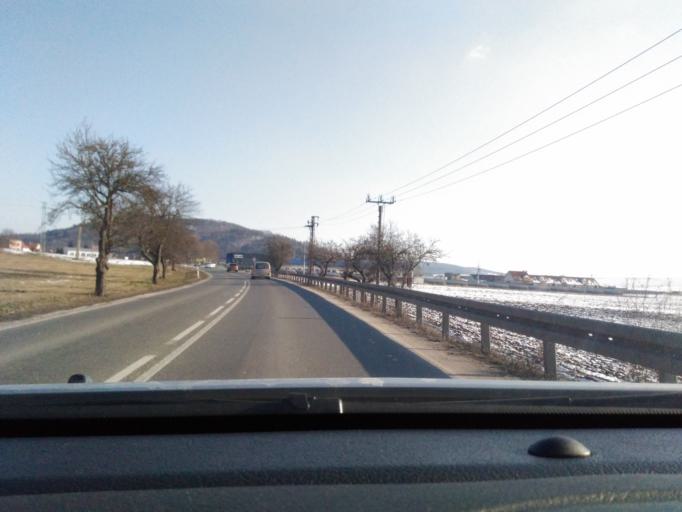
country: CZ
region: South Moravian
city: Kurim
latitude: 49.3020
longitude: 16.5144
